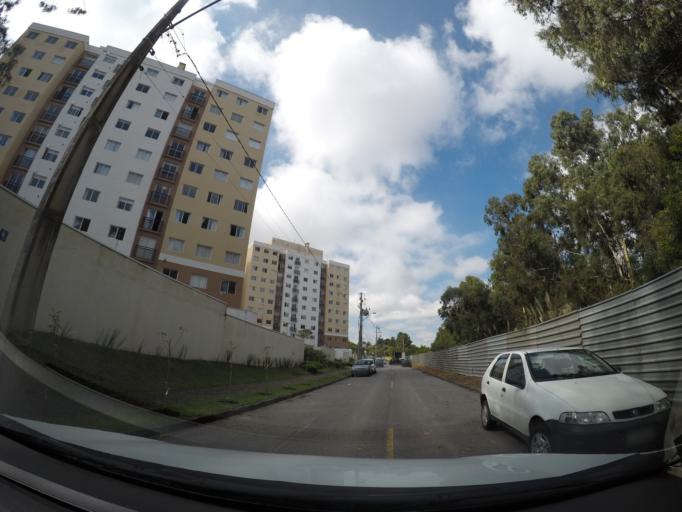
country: BR
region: Parana
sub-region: Sao Jose Dos Pinhais
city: Sao Jose dos Pinhais
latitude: -25.4874
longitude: -49.2207
